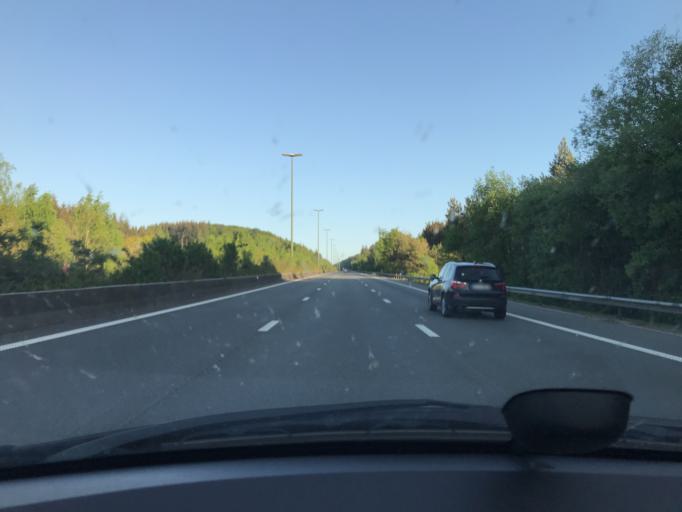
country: BE
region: Wallonia
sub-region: Province du Luxembourg
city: Tellin
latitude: 50.0779
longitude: 5.1746
